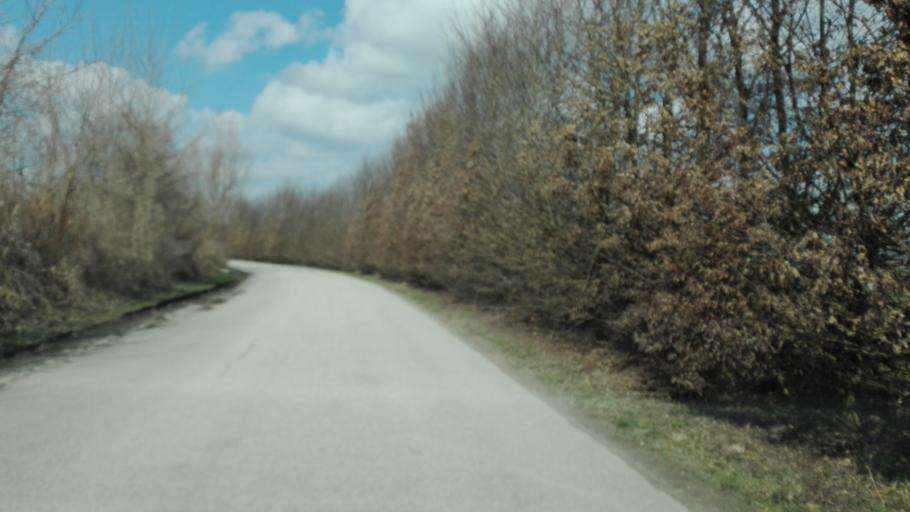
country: AT
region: Upper Austria
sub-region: Politischer Bezirk Urfahr-Umgebung
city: Feldkirchen an der Donau
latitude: 48.3304
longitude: 14.0650
